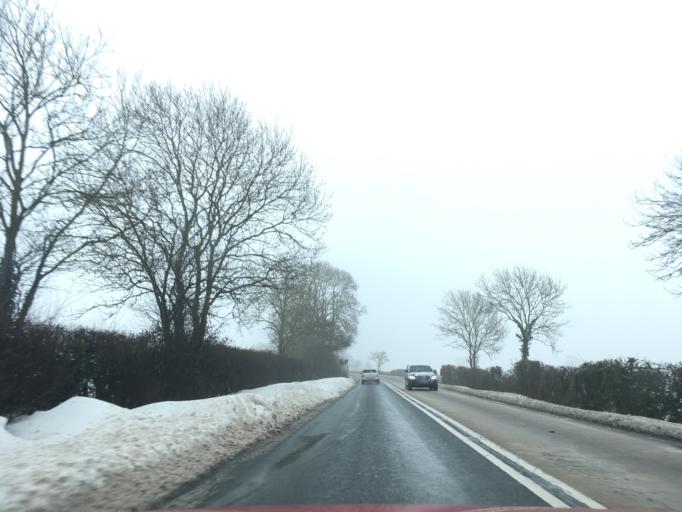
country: GB
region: England
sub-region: Warwickshire
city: Bidford-on-avon
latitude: 52.2022
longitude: -1.7911
